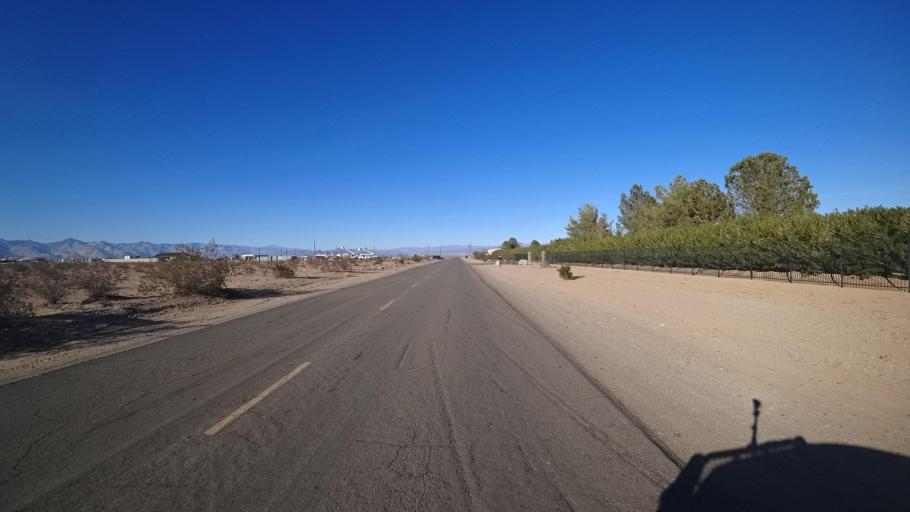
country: US
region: California
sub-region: Kern County
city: Ridgecrest
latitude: 35.6483
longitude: -117.7056
